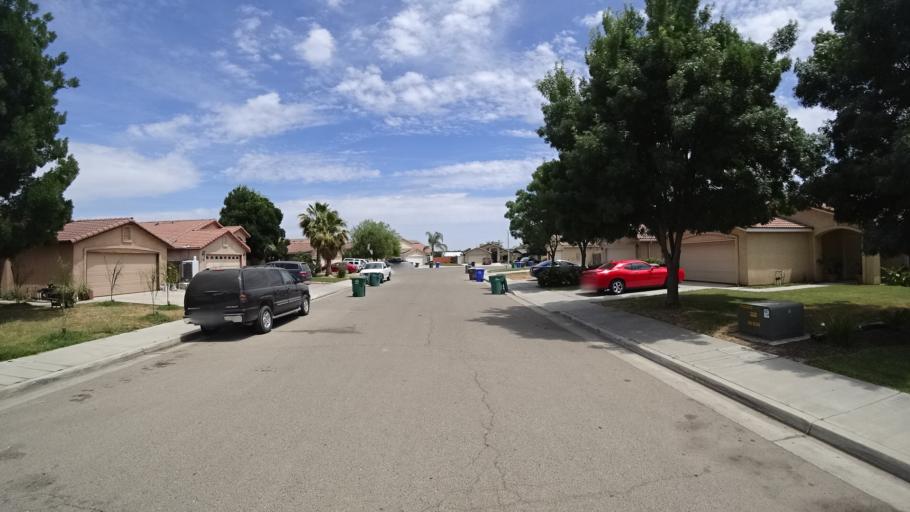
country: US
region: California
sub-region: Kings County
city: Armona
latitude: 36.3198
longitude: -119.6999
